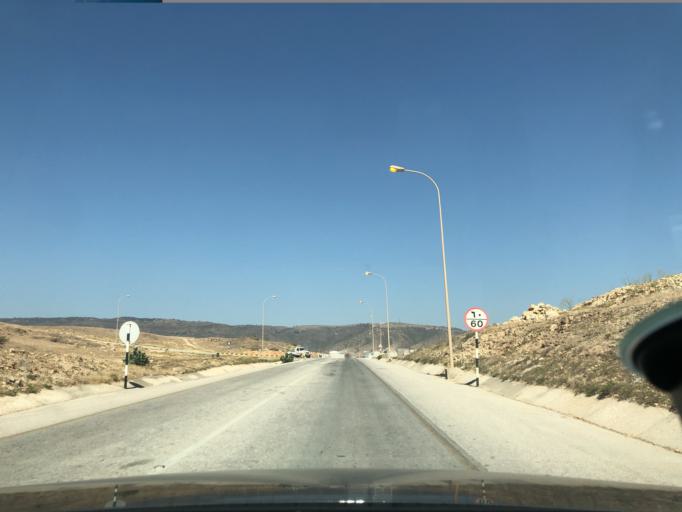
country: OM
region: Zufar
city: Salalah
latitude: 17.0416
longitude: 54.3990
